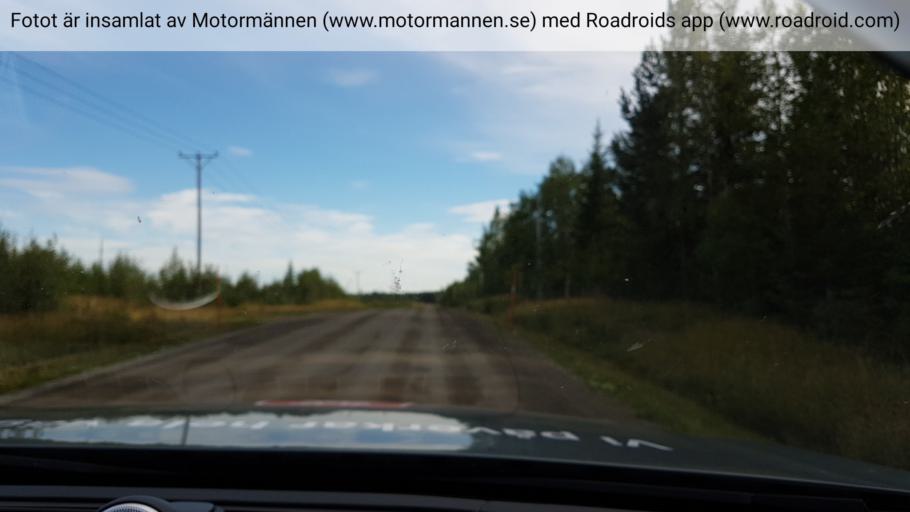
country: SE
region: Jaemtland
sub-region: Stroemsunds Kommun
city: Stroemsund
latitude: 63.9942
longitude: 15.8158
